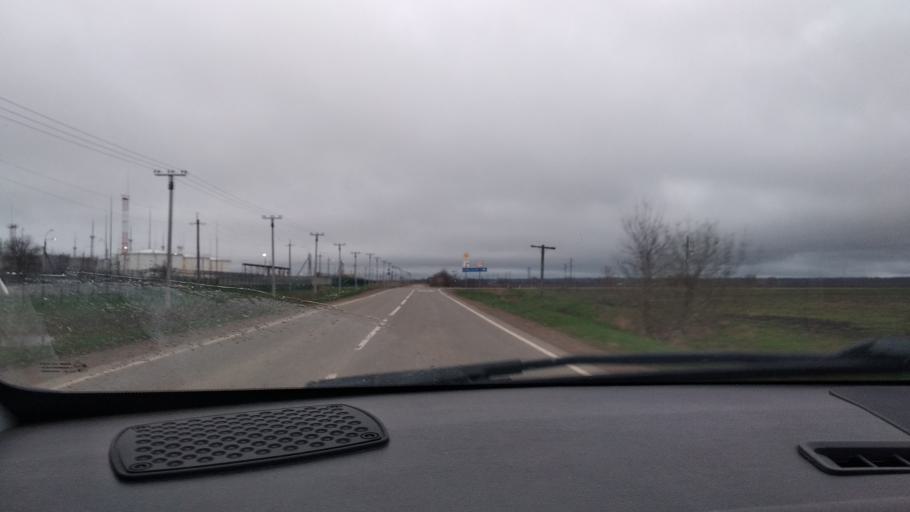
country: RU
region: Krasnodarskiy
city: Afipskiy
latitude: 44.8916
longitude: 38.8019
